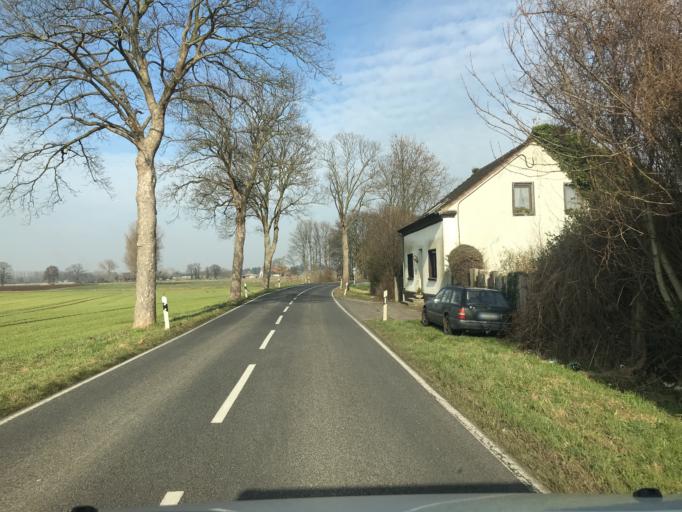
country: DE
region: North Rhine-Westphalia
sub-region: Regierungsbezirk Dusseldorf
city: Viersen
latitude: 51.3037
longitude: 6.3882
